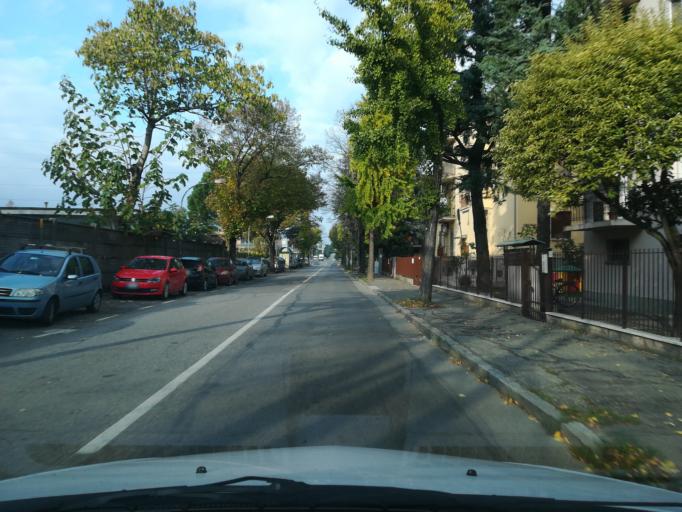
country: IT
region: Emilia-Romagna
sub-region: Provincia di Bologna
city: Imola
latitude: 44.3634
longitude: 11.7175
